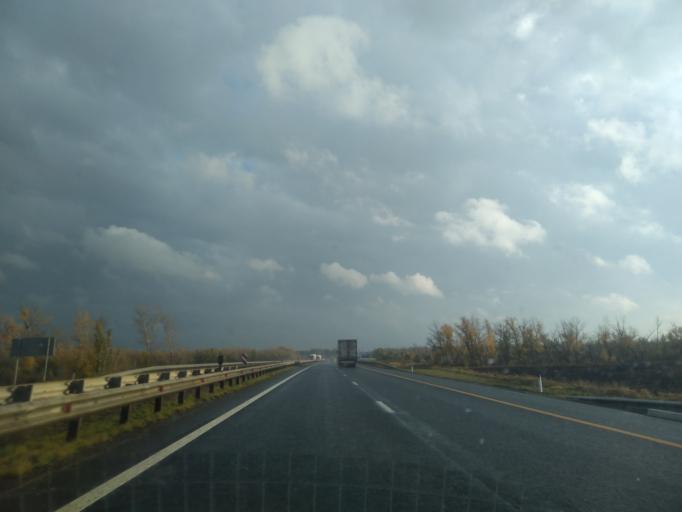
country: RU
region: Lipetsk
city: Yelets
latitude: 52.5573
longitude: 38.7145
